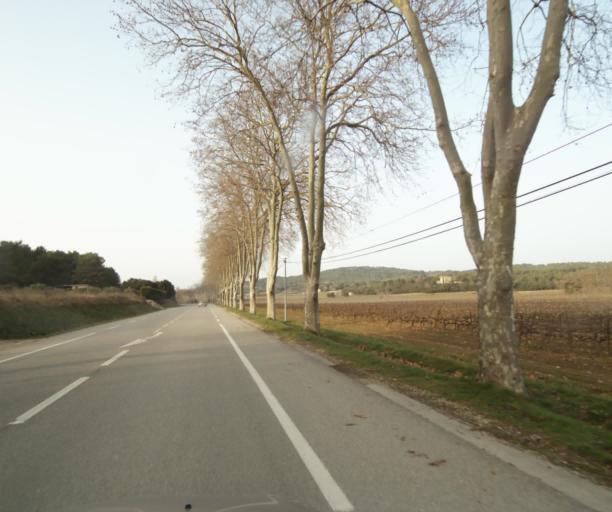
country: FR
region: Provence-Alpes-Cote d'Azur
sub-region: Departement des Bouches-du-Rhone
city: Rognes
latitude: 43.6495
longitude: 5.3580
